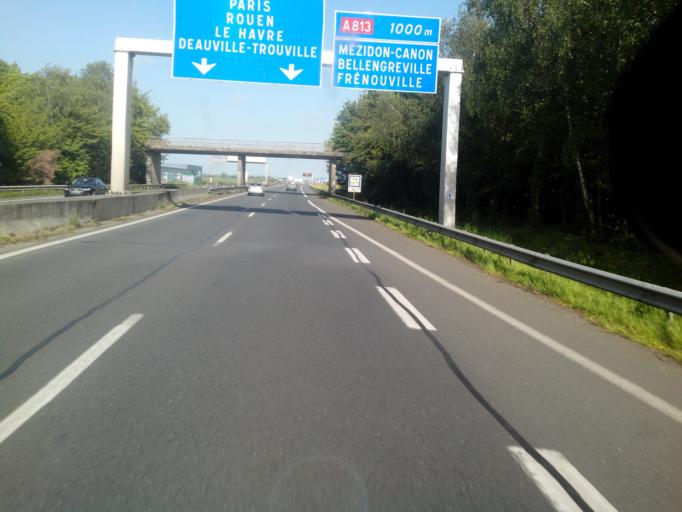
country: FR
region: Lower Normandy
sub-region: Departement du Calvados
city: Demouville
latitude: 49.1679
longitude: -0.2677
